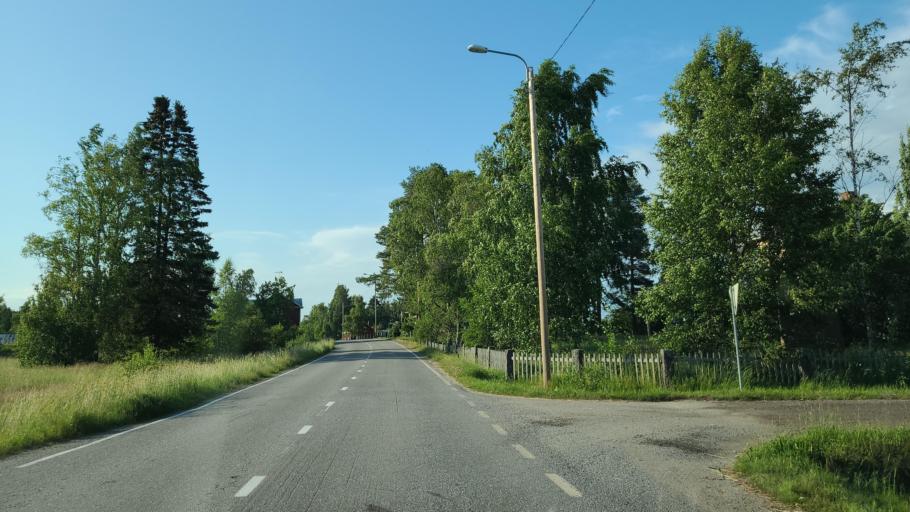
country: FI
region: Ostrobothnia
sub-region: Vaasa
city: Replot
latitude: 63.3381
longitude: 21.3316
